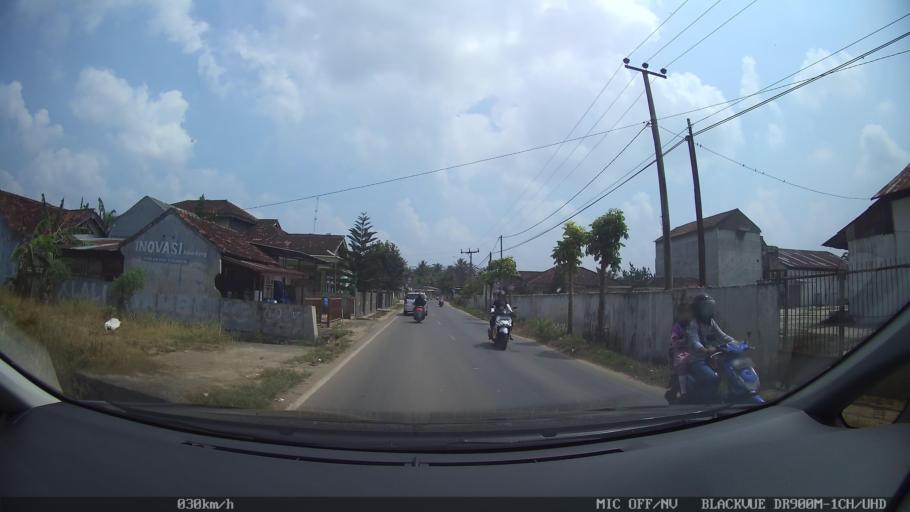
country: ID
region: Lampung
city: Pringsewu
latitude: -5.3711
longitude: 104.9662
